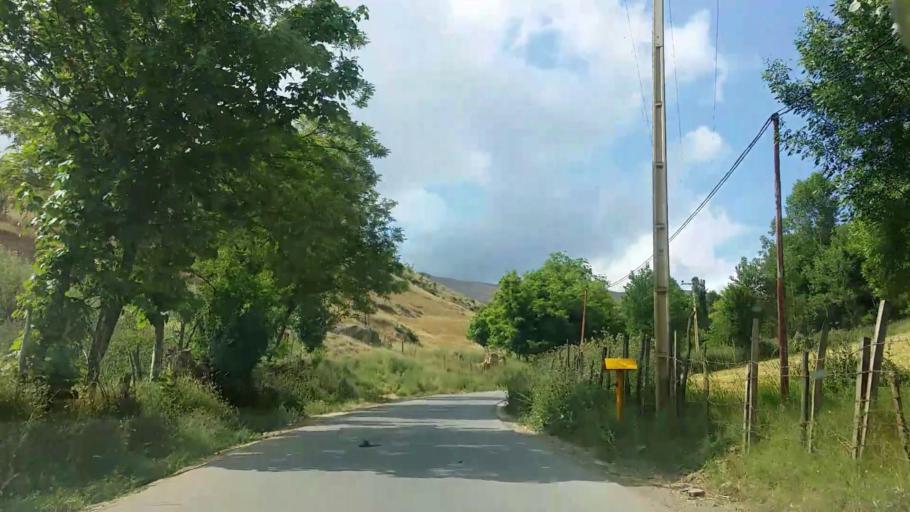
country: IR
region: Mazandaran
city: Chalus
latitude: 36.5184
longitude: 51.2597
